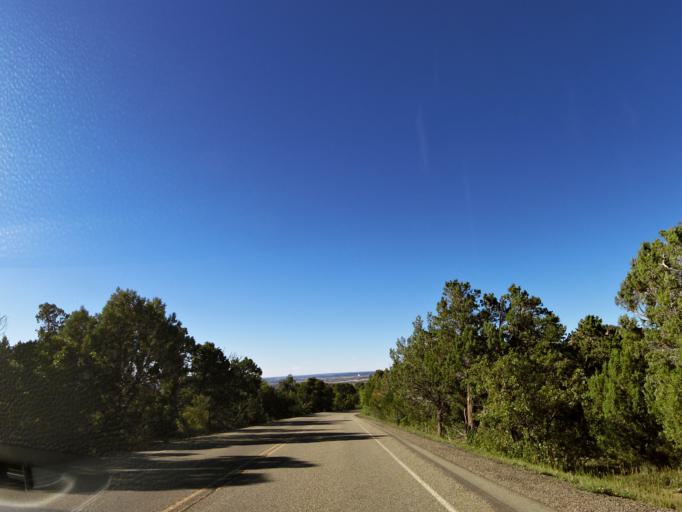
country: US
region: Colorado
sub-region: Montezuma County
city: Mancos
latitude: 37.3272
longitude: -108.4177
